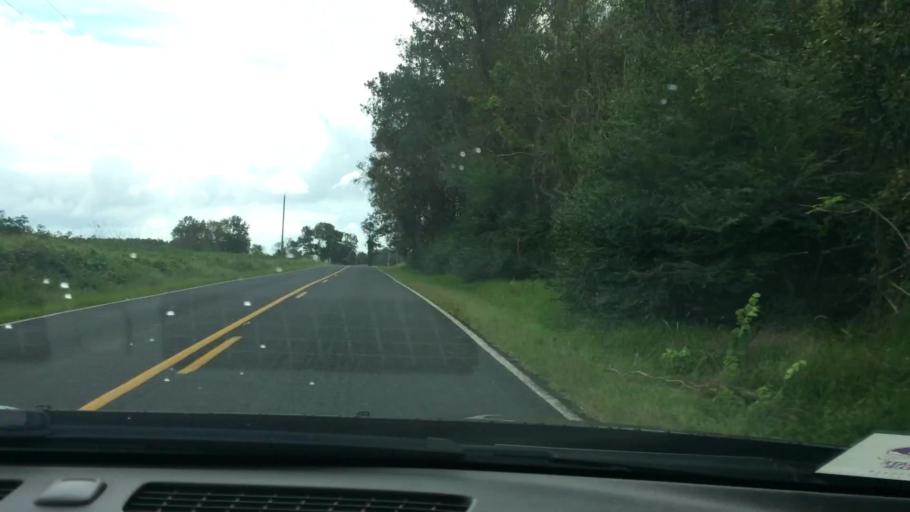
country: US
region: North Carolina
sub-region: Greene County
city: Maury
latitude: 35.4934
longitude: -77.5207
